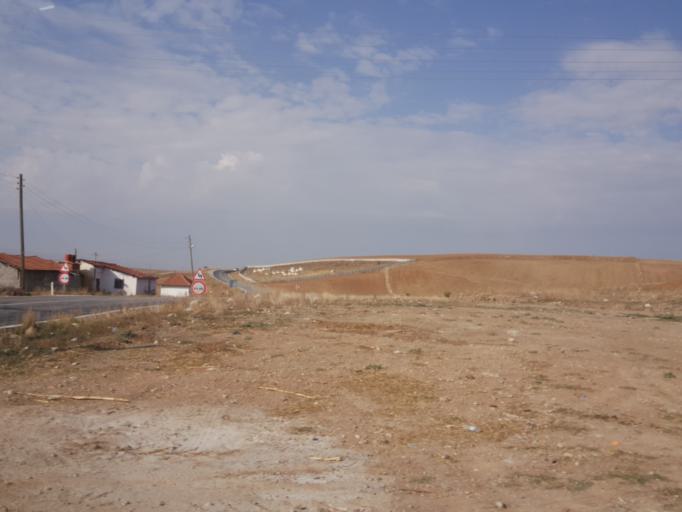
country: TR
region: Corum
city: Cemilbey
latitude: 40.1772
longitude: 35.0308
